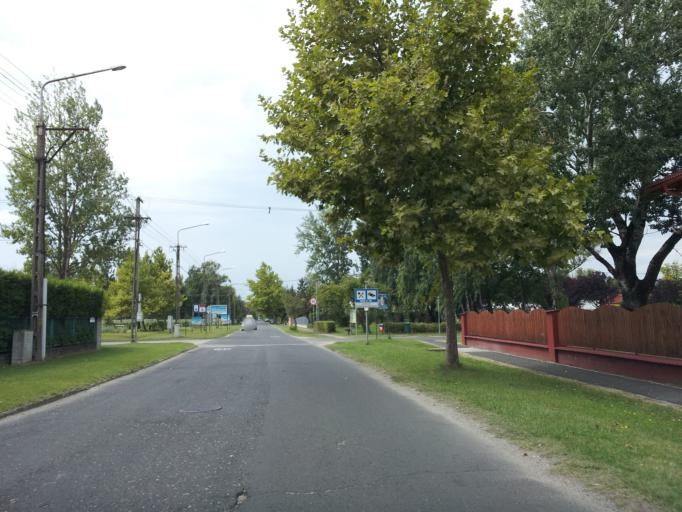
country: HU
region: Somogy
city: Zamardi
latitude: 46.8897
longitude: 17.9734
